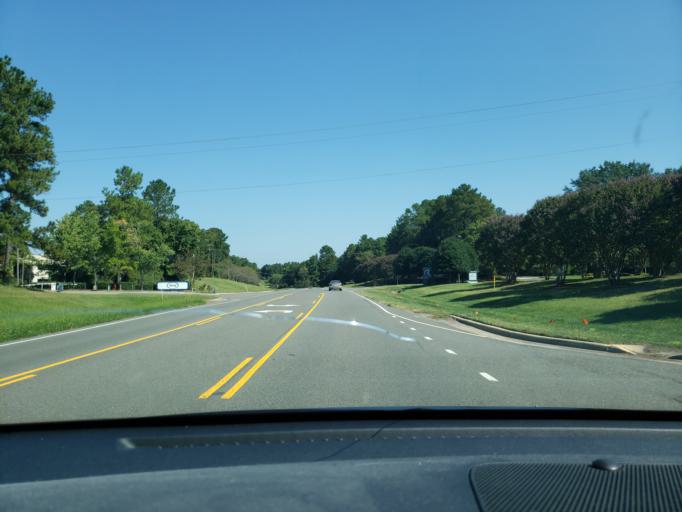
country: US
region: North Carolina
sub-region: Durham County
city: Durham
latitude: 35.9060
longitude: -78.8783
